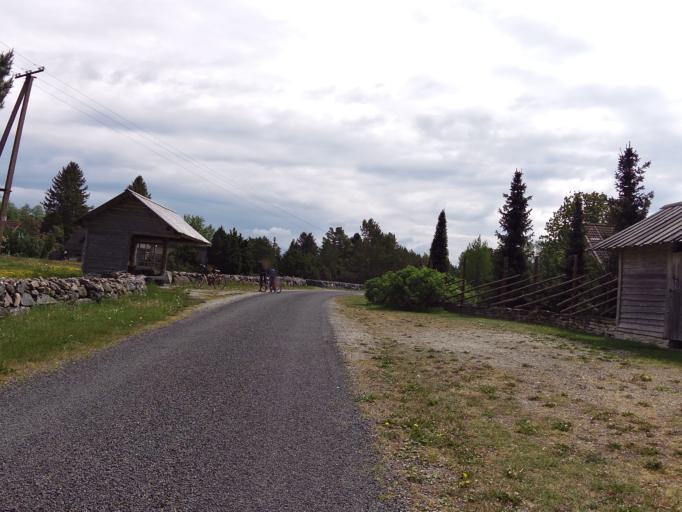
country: EE
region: Harju
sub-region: Paldiski linn
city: Paldiski
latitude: 59.2560
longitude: 23.7476
